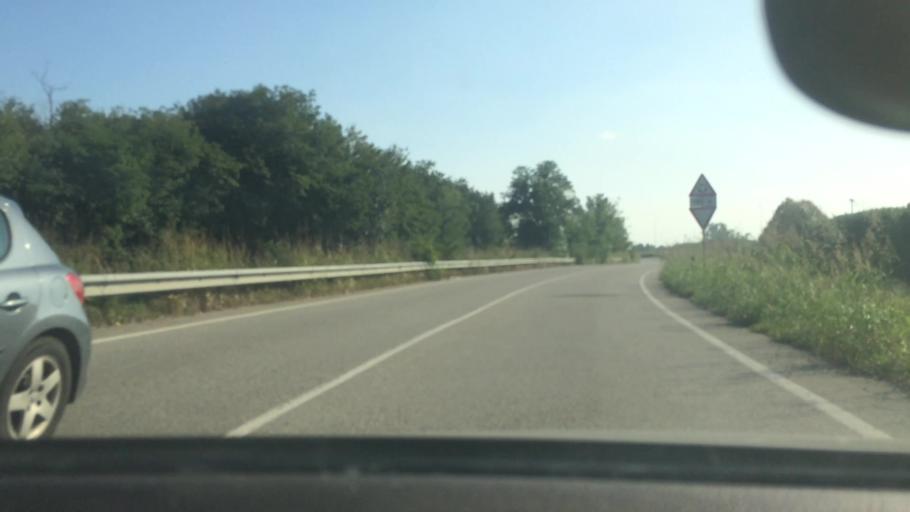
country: IT
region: Lombardy
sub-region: Citta metropolitana di Milano
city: Buscate
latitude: 45.5362
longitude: 8.8183
